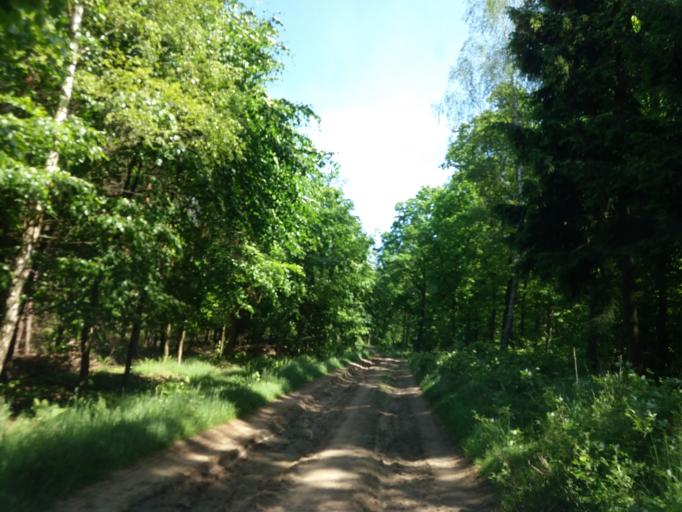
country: PL
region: West Pomeranian Voivodeship
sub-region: Powiat choszczenski
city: Recz
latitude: 53.3181
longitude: 15.5236
